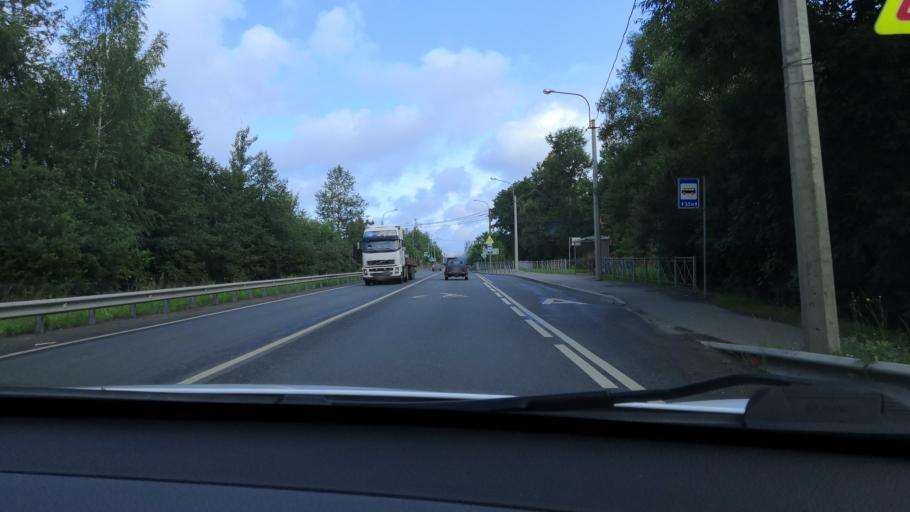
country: RU
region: St.-Petersburg
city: Tyarlevo
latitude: 59.7005
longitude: 30.4408
